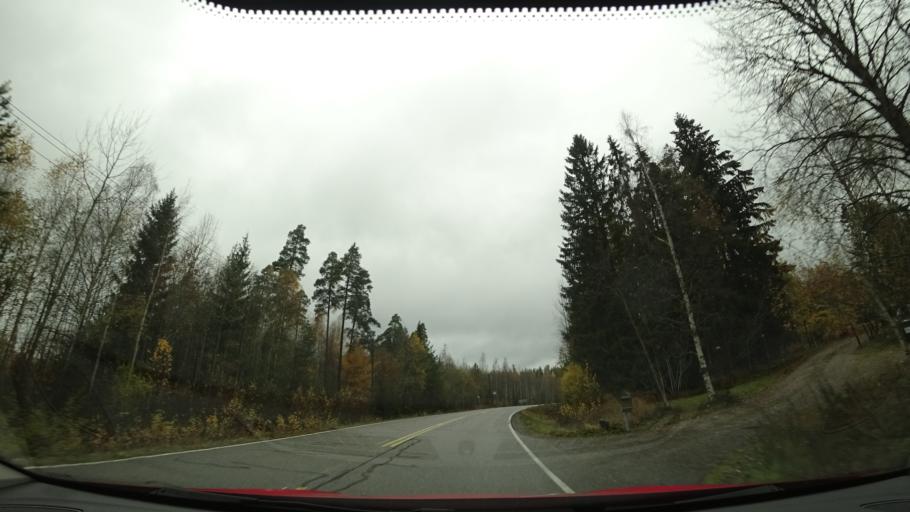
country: FI
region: Uusimaa
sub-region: Helsinki
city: Sibbo
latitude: 60.2814
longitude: 25.1963
